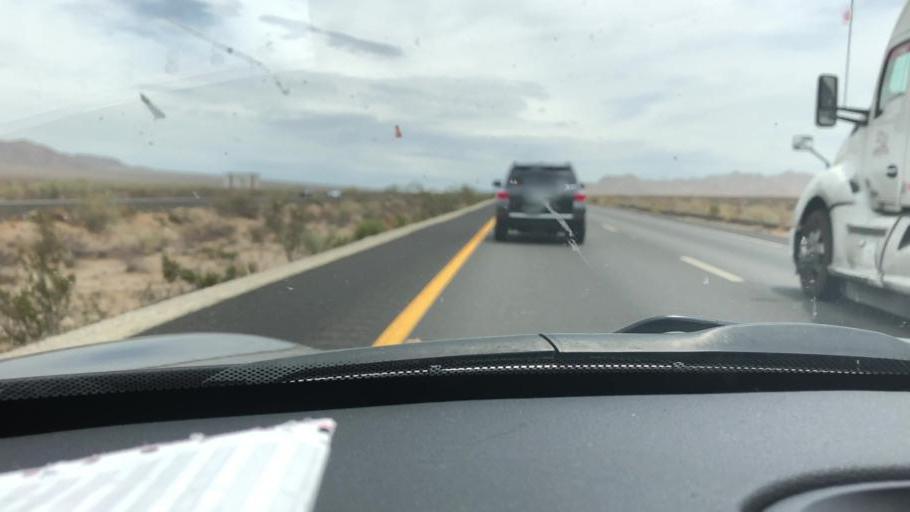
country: US
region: California
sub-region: Riverside County
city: Mecca
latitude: 33.6600
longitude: -115.7810
